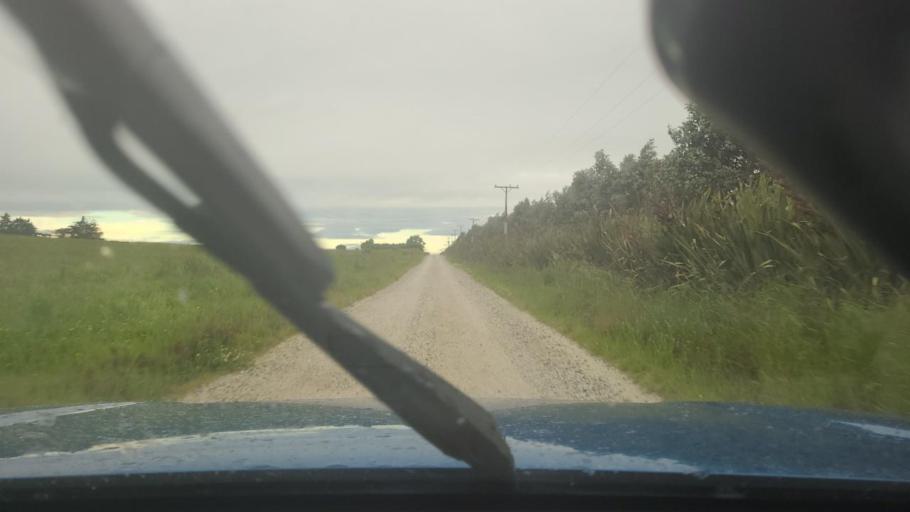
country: NZ
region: Southland
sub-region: Invercargill City
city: Invercargill
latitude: -46.4456
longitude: 168.5405
